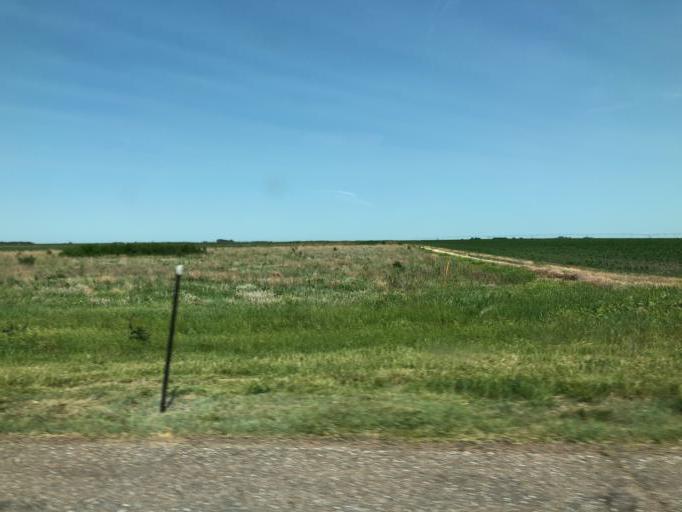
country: US
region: Nebraska
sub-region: Thayer County
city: Hebron
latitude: 40.3139
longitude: -97.5764
